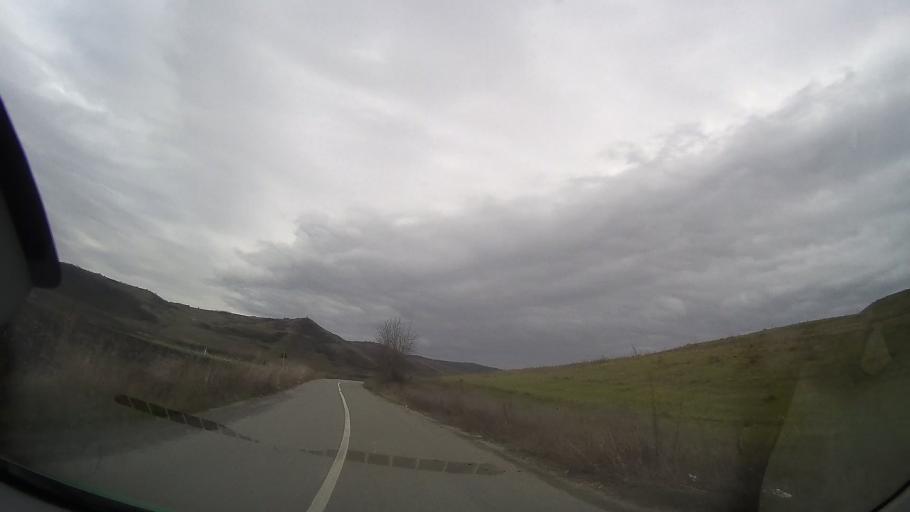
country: RO
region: Mures
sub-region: Comuna Craesti
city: Craiesti
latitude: 46.7837
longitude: 24.4253
